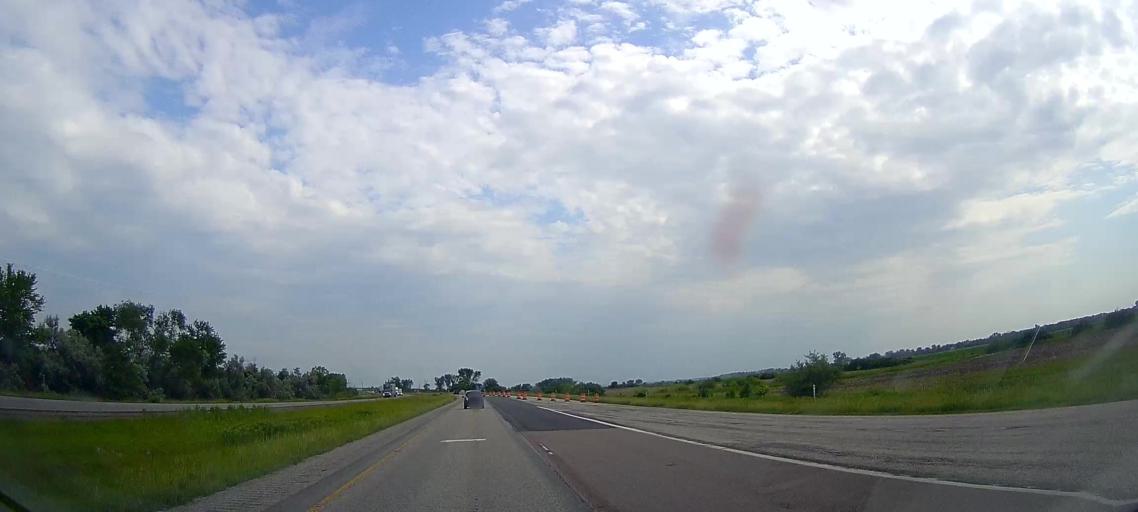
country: US
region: Nebraska
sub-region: Burt County
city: Tekamah
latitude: 41.7382
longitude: -96.0482
